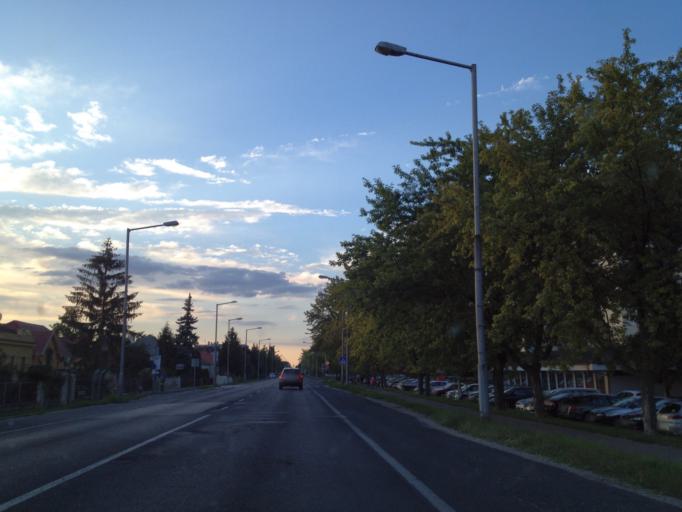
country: HU
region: Gyor-Moson-Sopron
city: Mosonmagyarovar
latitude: 47.8624
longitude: 17.2742
